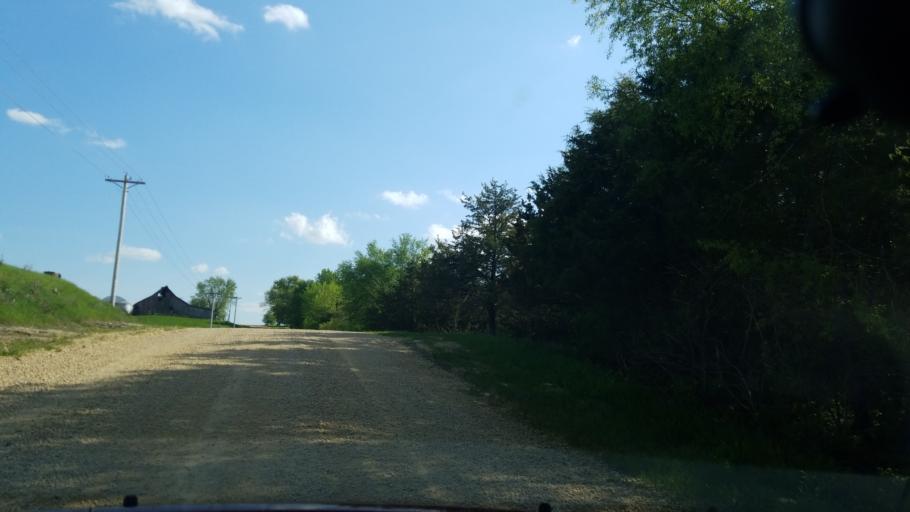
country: US
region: Iowa
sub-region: Jackson County
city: Maquoketa
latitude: 42.2095
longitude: -90.7295
